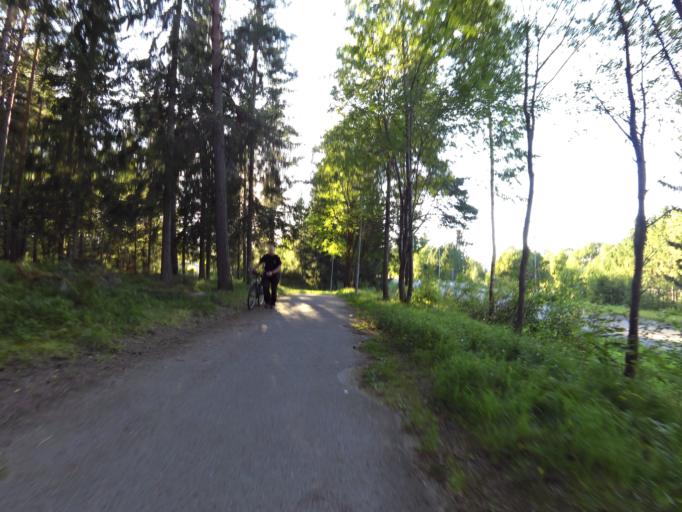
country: SE
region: Gaevleborg
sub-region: Gavle Kommun
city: Gavle
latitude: 60.6552
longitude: 17.1413
